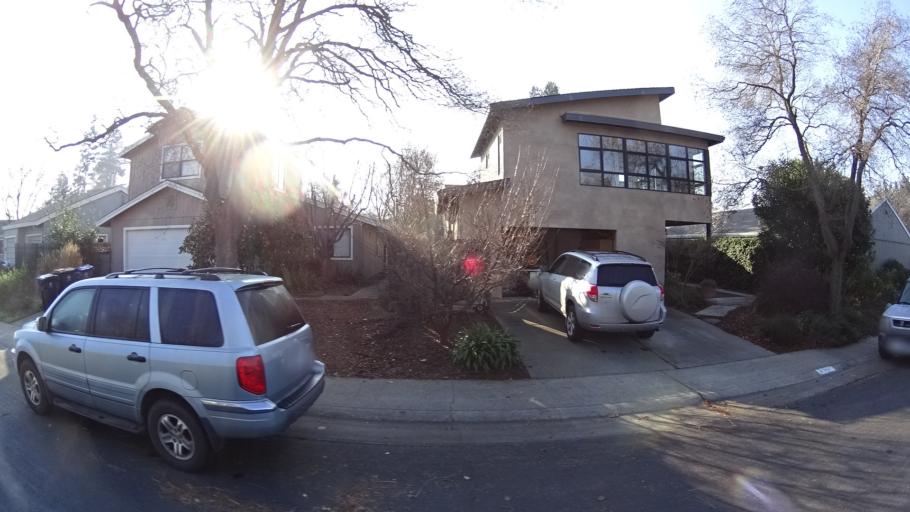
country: US
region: California
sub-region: Yolo County
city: Davis
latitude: 38.5579
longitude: -121.7915
